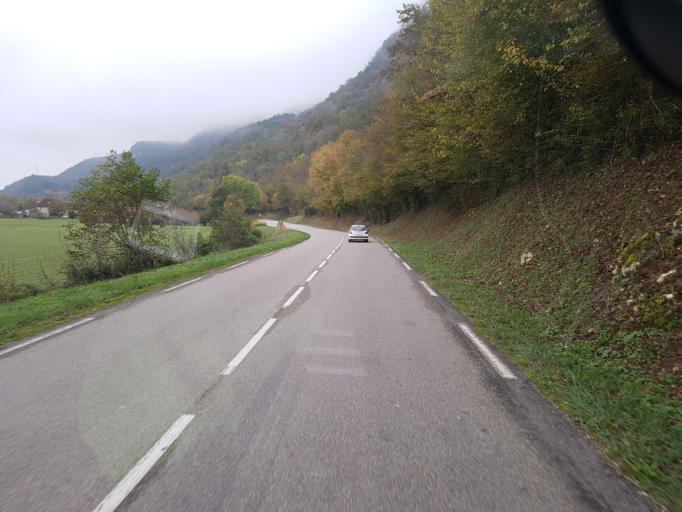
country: FR
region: Rhone-Alpes
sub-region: Departement de la Savoie
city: Yenne
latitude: 45.6633
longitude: 5.7038
